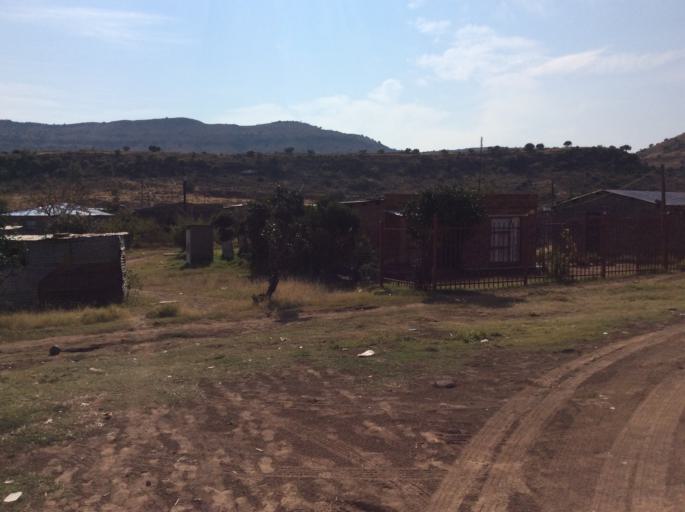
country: LS
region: Mafeteng
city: Mafeteng
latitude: -29.7187
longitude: 27.0332
